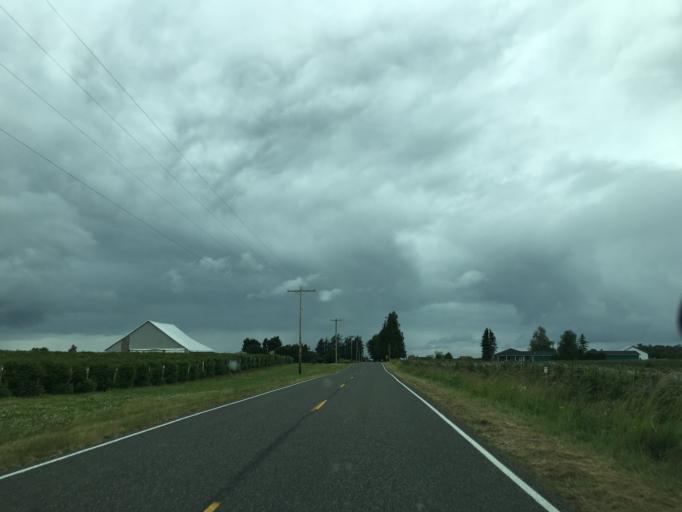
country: US
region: Washington
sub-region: Whatcom County
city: Everson
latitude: 48.9820
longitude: -122.3607
